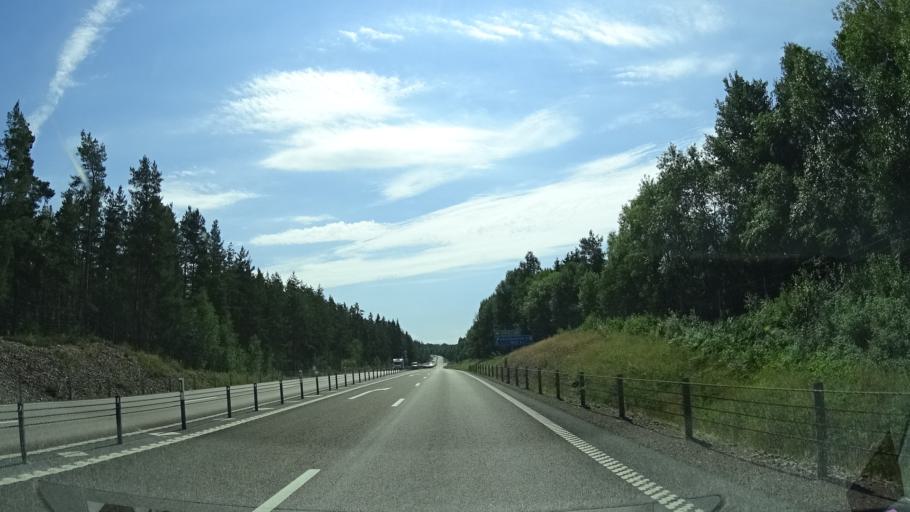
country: SE
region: Vaermland
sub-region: Kristinehamns Kommun
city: Kristinehamn
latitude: 59.3358
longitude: 14.0931
